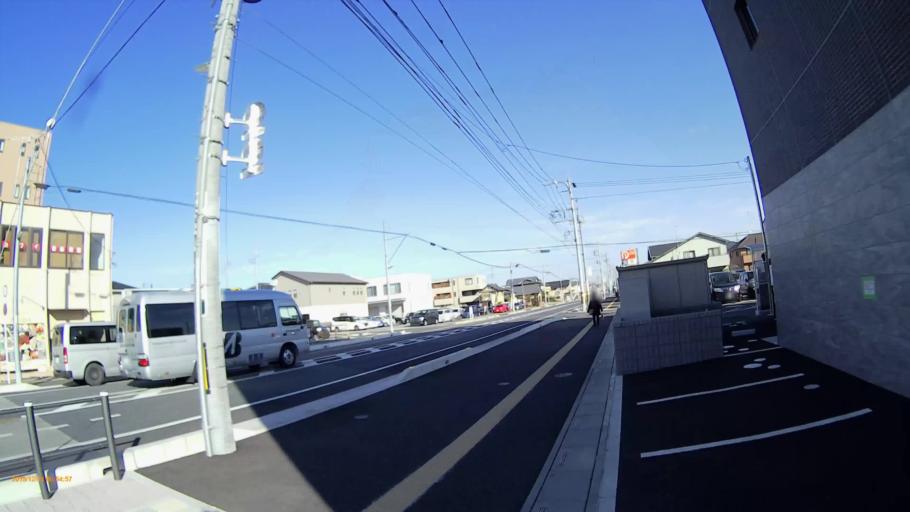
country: JP
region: Saitama
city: Fukayacho
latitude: 36.1750
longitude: 139.3311
